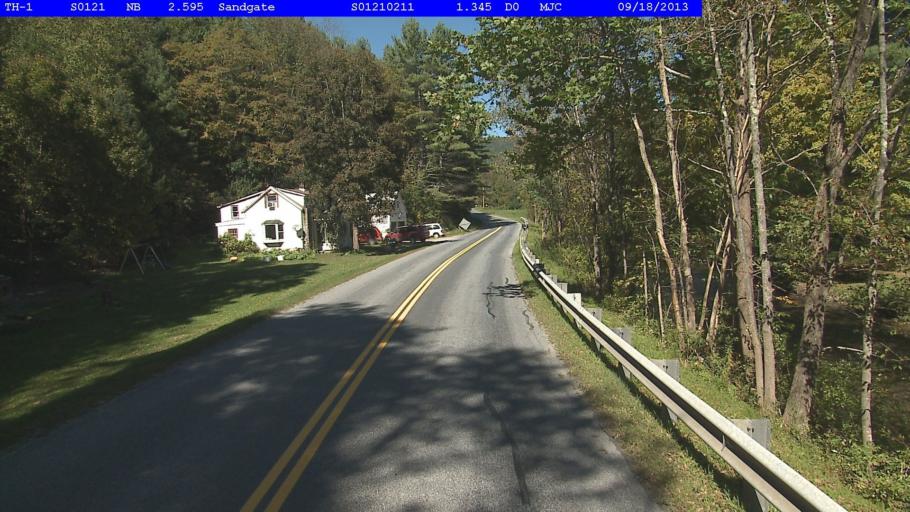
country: US
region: Vermont
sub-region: Bennington County
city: Arlington
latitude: 43.1394
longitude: -73.2039
